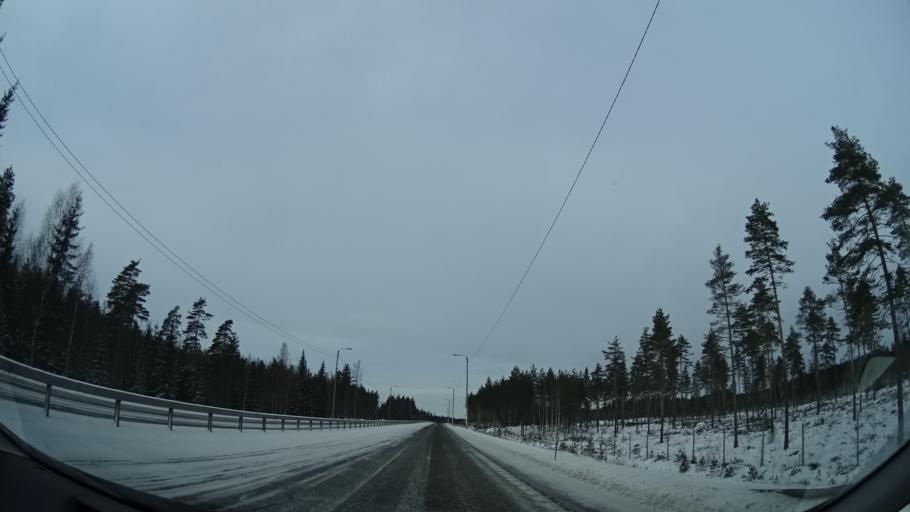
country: FI
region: Uusimaa
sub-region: Helsinki
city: Kaerkoelae
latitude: 60.6346
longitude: 23.9074
